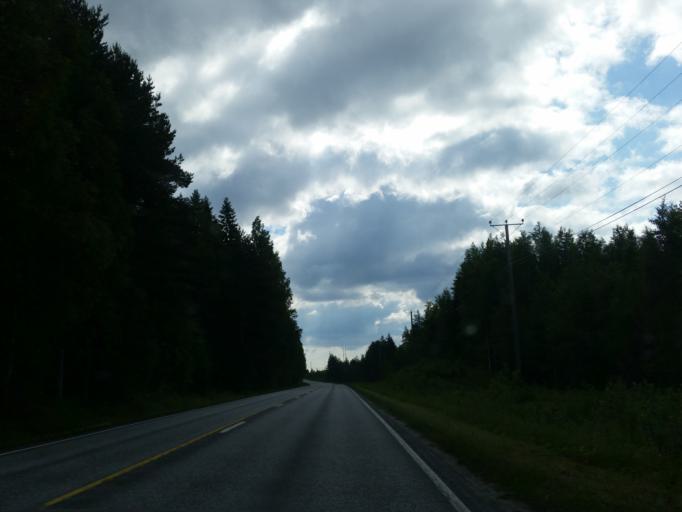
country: FI
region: Northern Savo
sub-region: Kuopio
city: Kuopio
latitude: 62.8439
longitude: 27.4714
